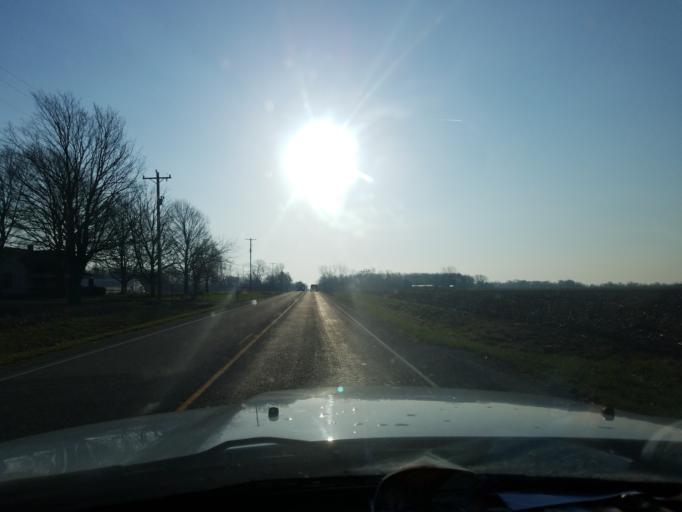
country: US
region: Indiana
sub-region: Vigo County
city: Seelyville
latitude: 39.3905
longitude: -87.2747
